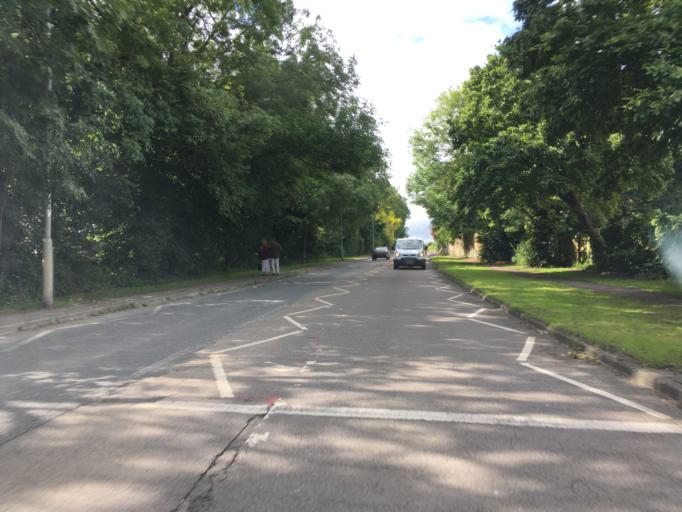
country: GB
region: England
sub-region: Borough of Swindon
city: Highworth
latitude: 51.6383
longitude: -1.7085
